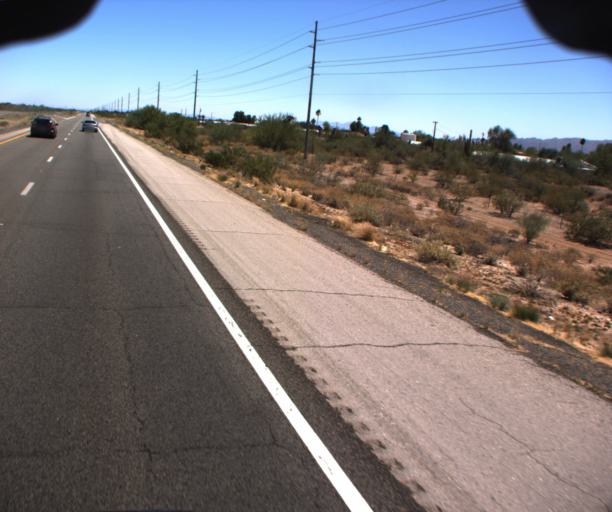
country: US
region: Arizona
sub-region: Maricopa County
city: Sun City West
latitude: 33.7907
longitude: -112.5453
